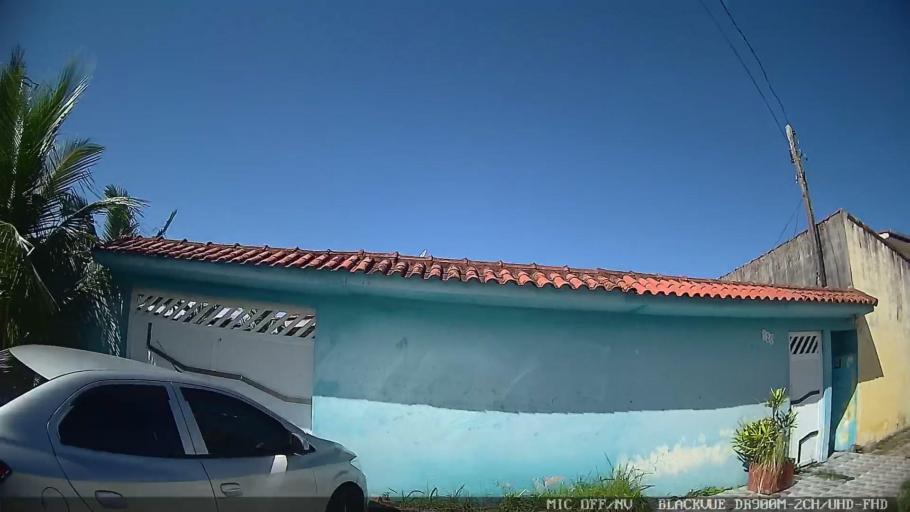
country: BR
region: Sao Paulo
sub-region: Iguape
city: Iguape
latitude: -24.6957
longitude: -47.5617
